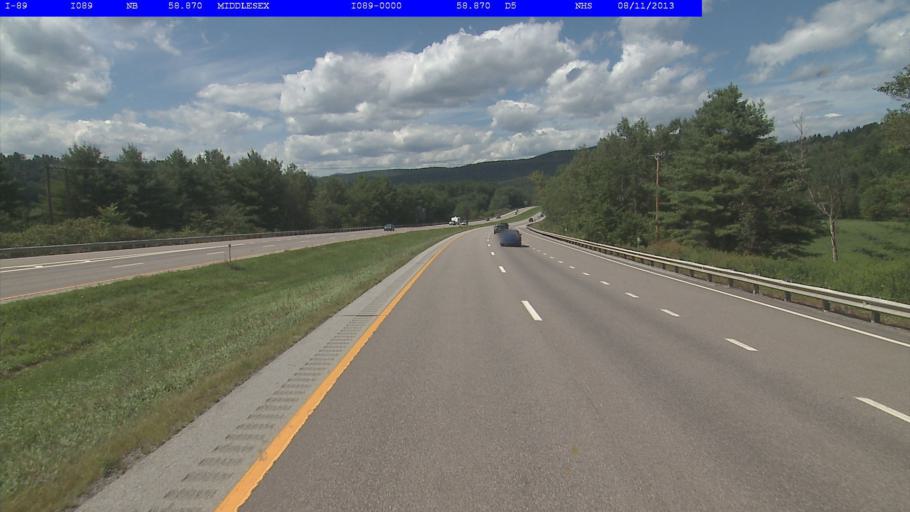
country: US
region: Vermont
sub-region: Washington County
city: Waterbury
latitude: 44.3000
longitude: -72.6873
